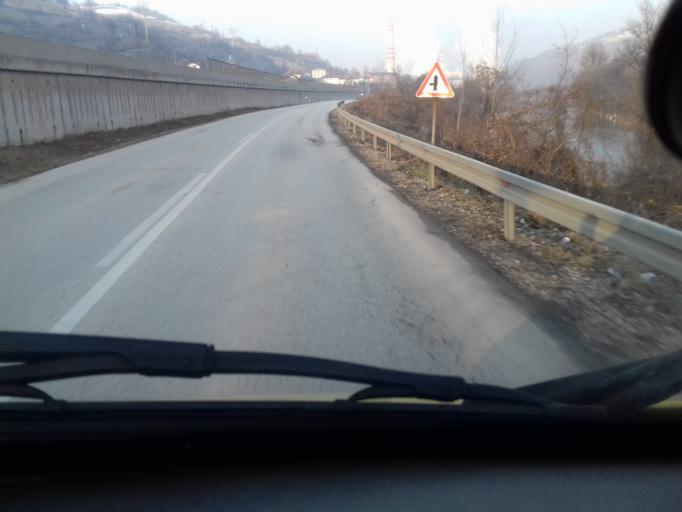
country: BA
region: Federation of Bosnia and Herzegovina
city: Dobrinje
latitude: 44.0758
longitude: 18.1085
